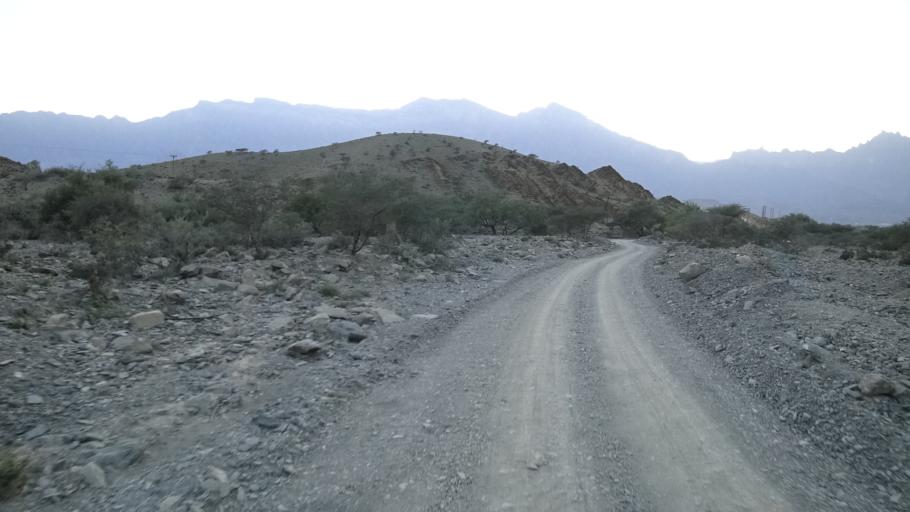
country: OM
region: Al Batinah
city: Rustaq
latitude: 23.2791
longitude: 57.3556
